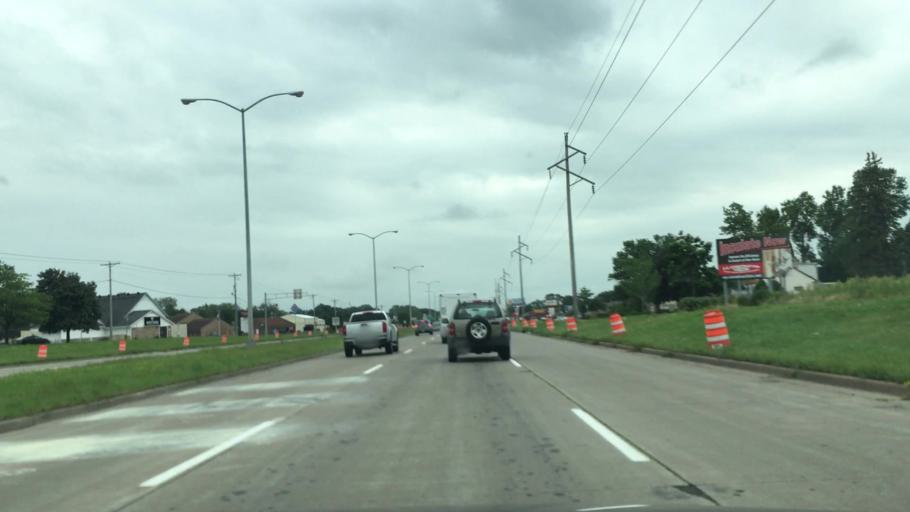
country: US
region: Wisconsin
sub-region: Eau Claire County
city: Eau Claire
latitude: 44.8185
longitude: -91.5425
